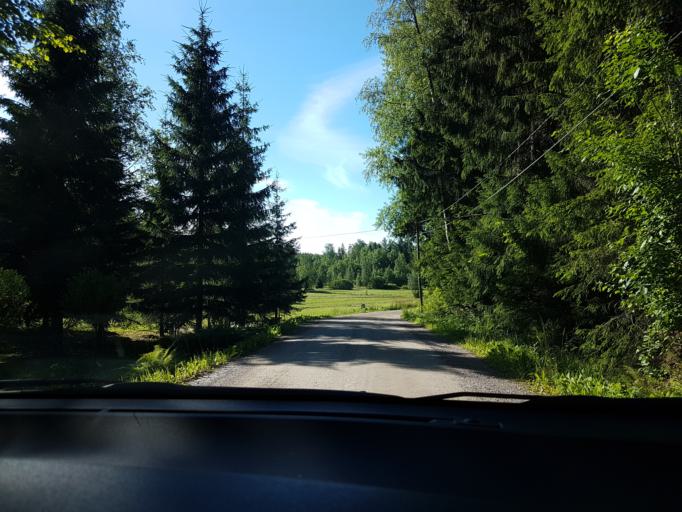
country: FI
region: Uusimaa
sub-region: Helsinki
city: Sibbo
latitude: 60.2873
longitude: 25.2397
